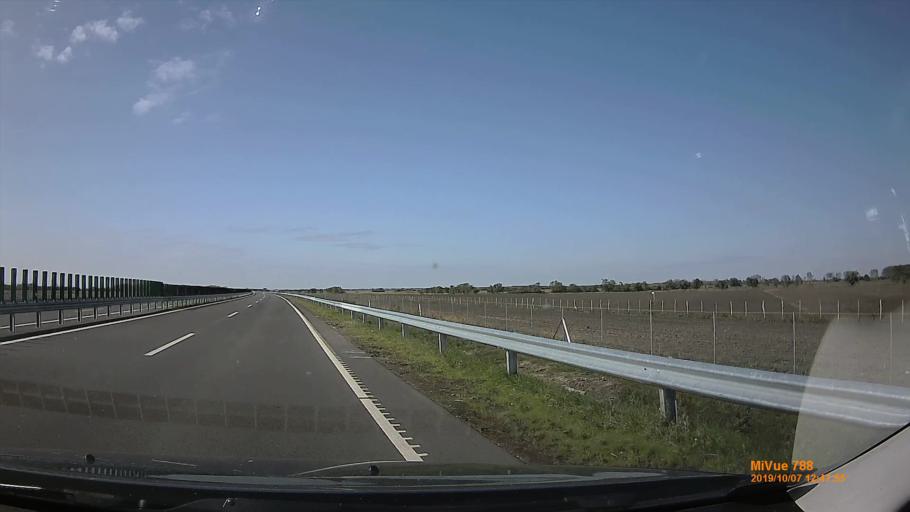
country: HU
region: Jasz-Nagykun-Szolnok
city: Cserkeszolo
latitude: 46.8826
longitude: 20.2326
